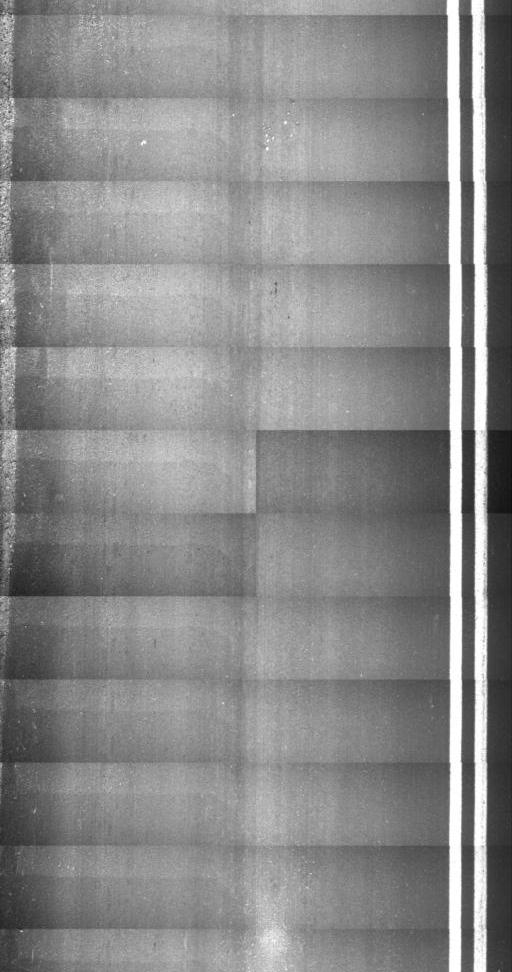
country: US
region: Vermont
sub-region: Windsor County
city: Woodstock
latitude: 43.5645
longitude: -72.5330
